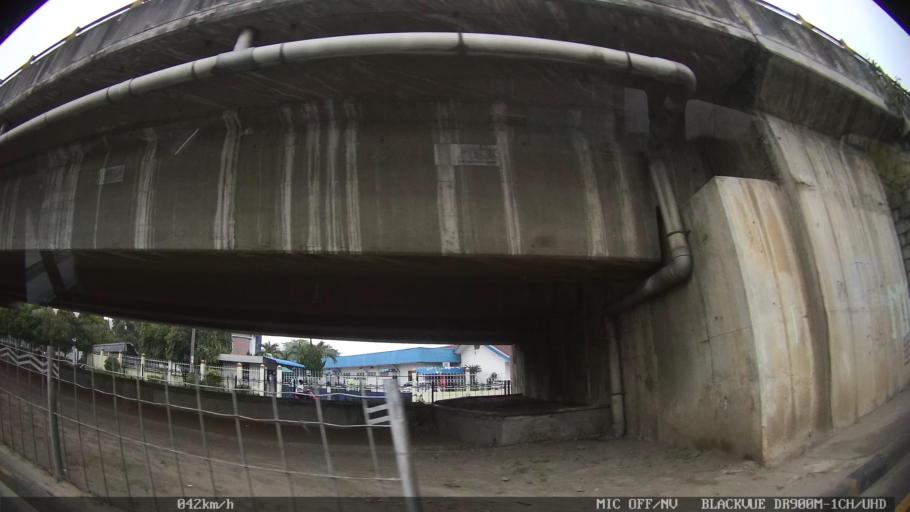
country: ID
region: North Sumatra
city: Deli Tua
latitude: 3.5341
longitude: 98.7225
